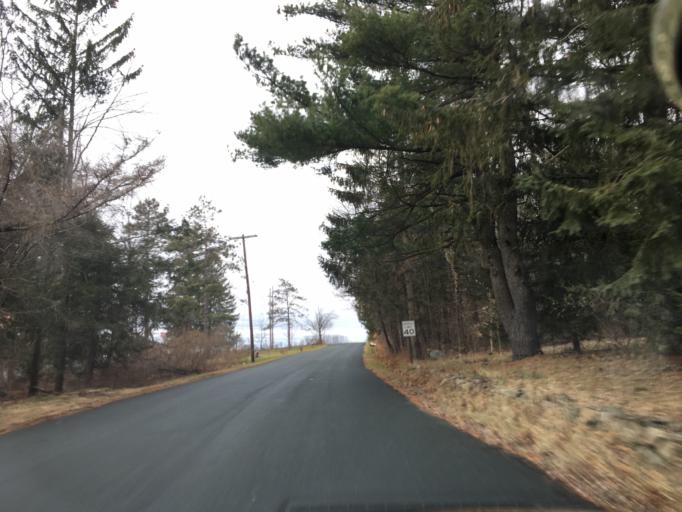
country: US
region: New York
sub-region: Rensselaer County
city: Averill Park
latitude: 42.6103
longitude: -73.5437
